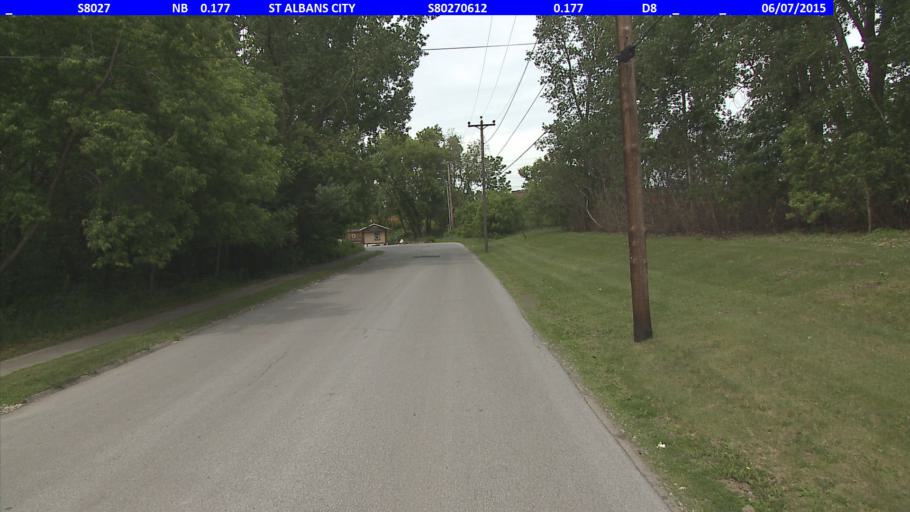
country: US
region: Vermont
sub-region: Franklin County
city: Saint Albans
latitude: 44.8136
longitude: -73.0881
